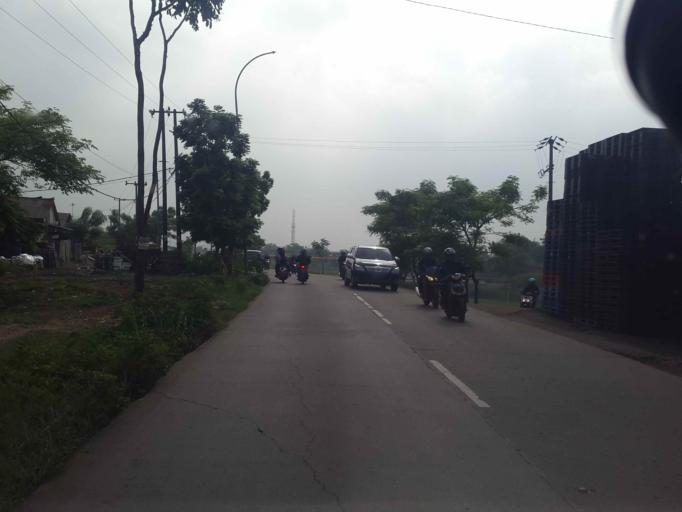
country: ID
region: West Java
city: Cikarang
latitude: -6.2949
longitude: 107.1201
